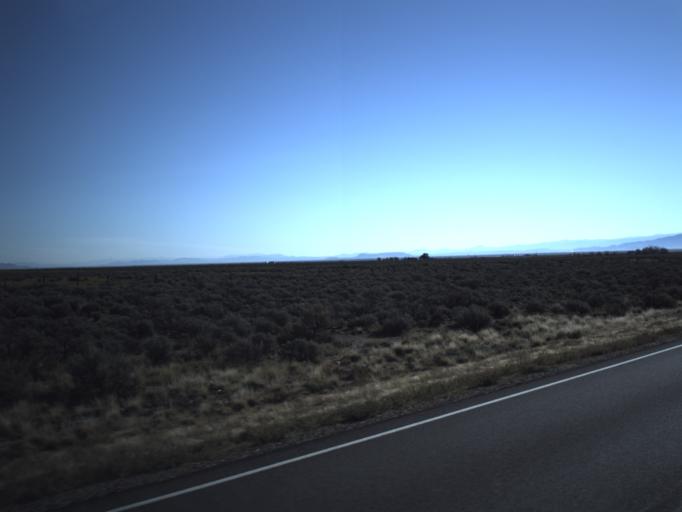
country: US
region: Utah
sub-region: Washington County
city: Enterprise
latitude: 37.7974
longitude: -113.9078
